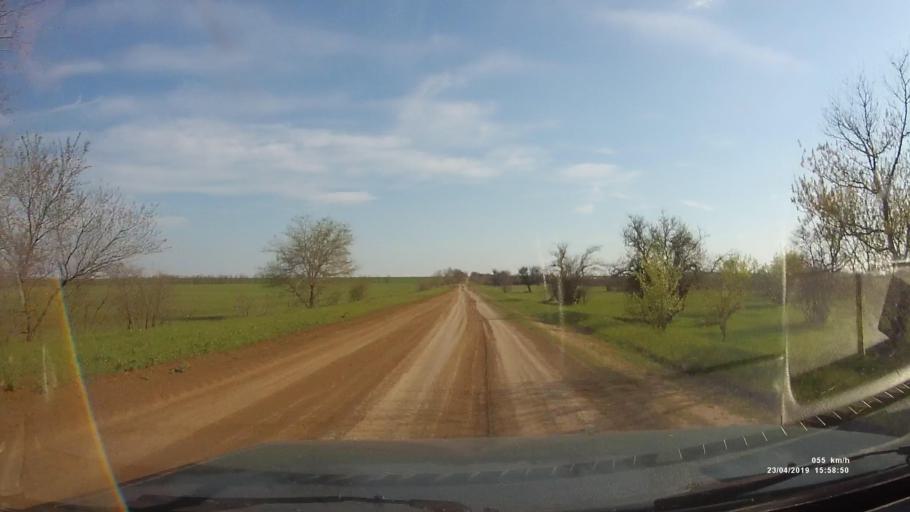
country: RU
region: Rostov
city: Remontnoye
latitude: 46.5210
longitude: 43.1095
